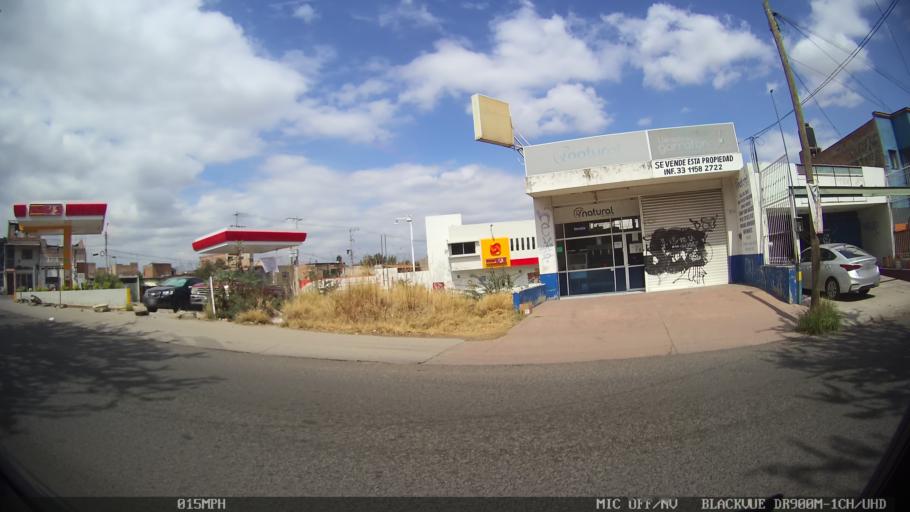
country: MX
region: Jalisco
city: Tonala
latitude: 20.6313
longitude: -103.2498
